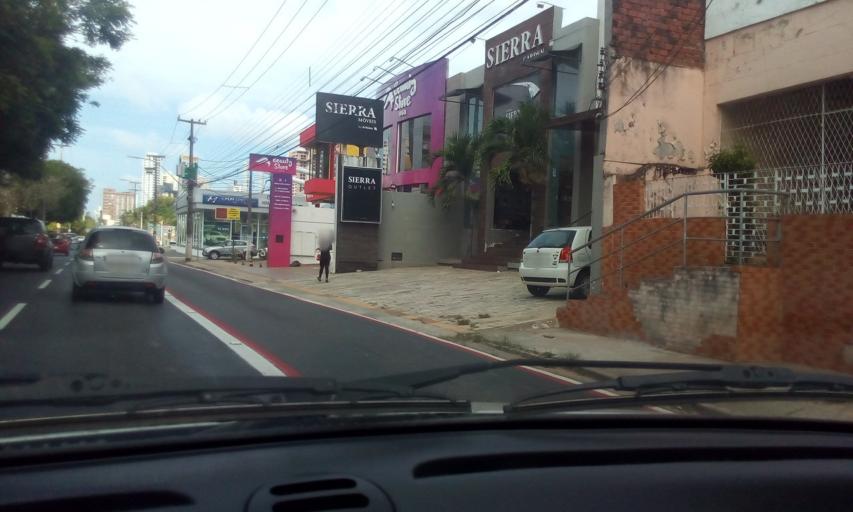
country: BR
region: Rio Grande do Norte
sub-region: Natal
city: Natal
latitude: -5.7986
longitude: -35.2052
